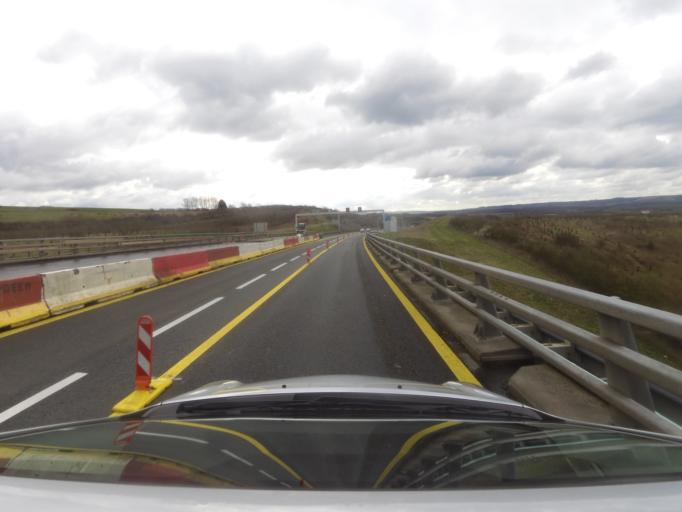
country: FR
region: Nord-Pas-de-Calais
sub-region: Departement du Pas-de-Calais
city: Isques
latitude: 50.6805
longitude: 1.6582
